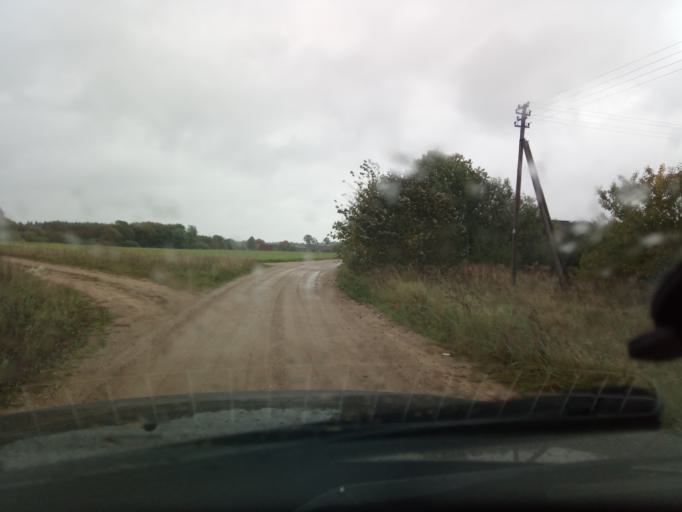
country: LT
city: Skaidiskes
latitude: 54.5948
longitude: 25.5758
